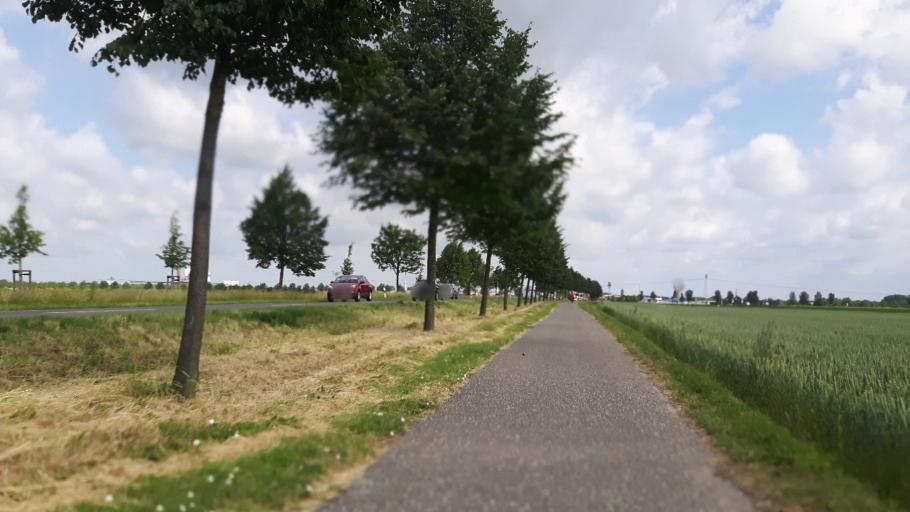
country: DE
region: Saxony
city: Dobernitz
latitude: 51.5042
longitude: 12.3396
